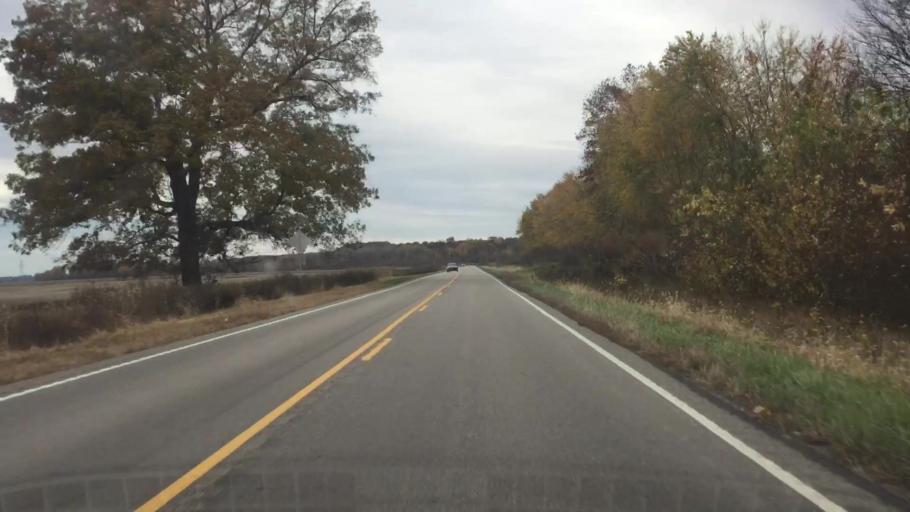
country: US
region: Missouri
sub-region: Osage County
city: Linn
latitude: 38.7072
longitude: -91.7470
